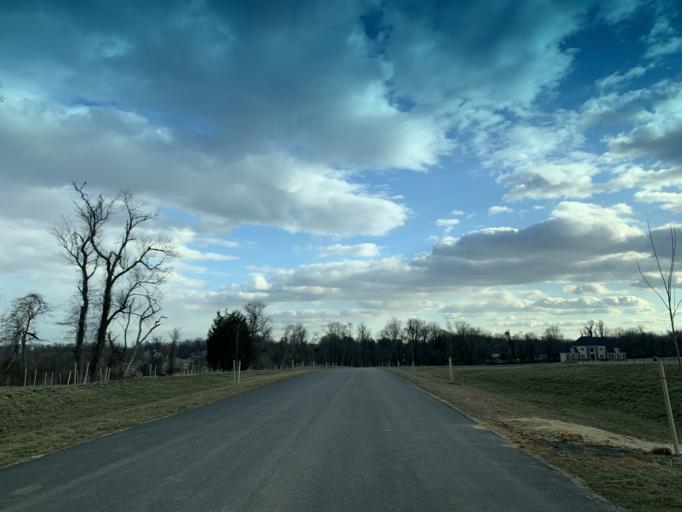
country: US
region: Maryland
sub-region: Harford County
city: Bel Air South
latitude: 39.4953
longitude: -76.2784
